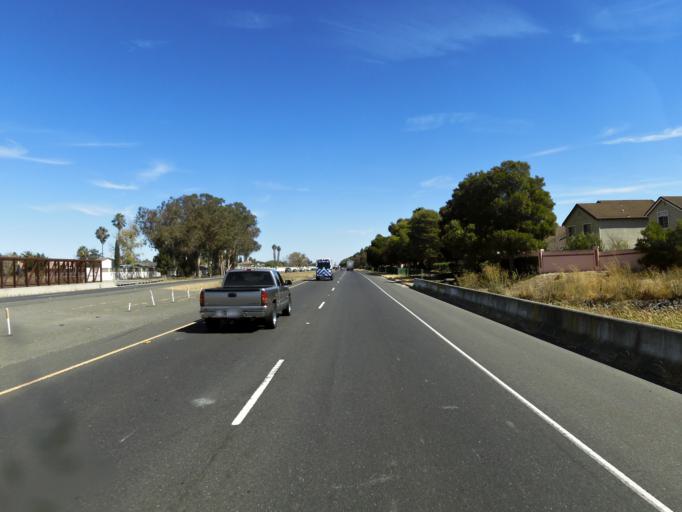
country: US
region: California
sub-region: Solano County
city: Fairfield
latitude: 38.2432
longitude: -122.0110
